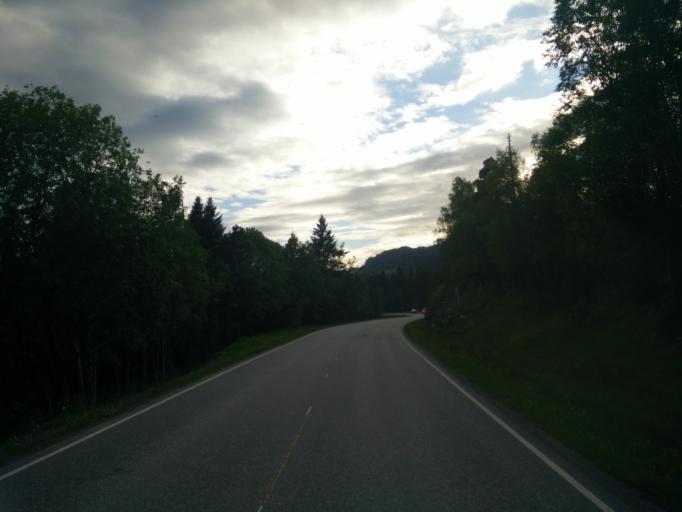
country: NO
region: More og Romsdal
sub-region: Tingvoll
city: Tingvoll
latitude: 63.0352
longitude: 8.0383
